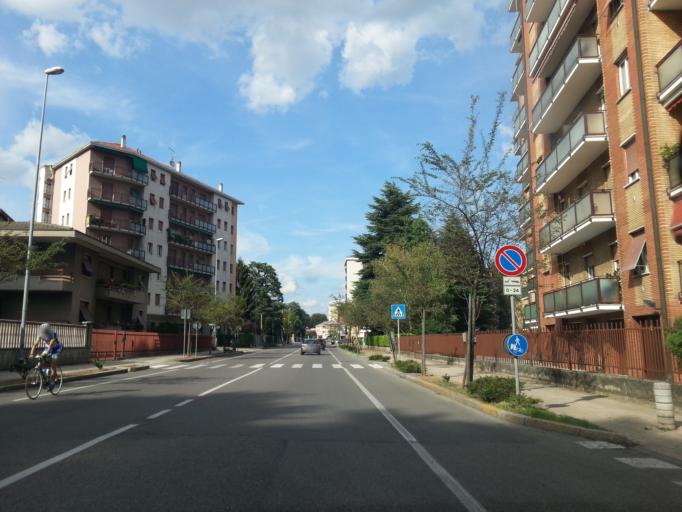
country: IT
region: Lombardy
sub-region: Provincia di Monza e Brianza
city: Vedano al Lambro
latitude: 45.6083
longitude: 9.2694
